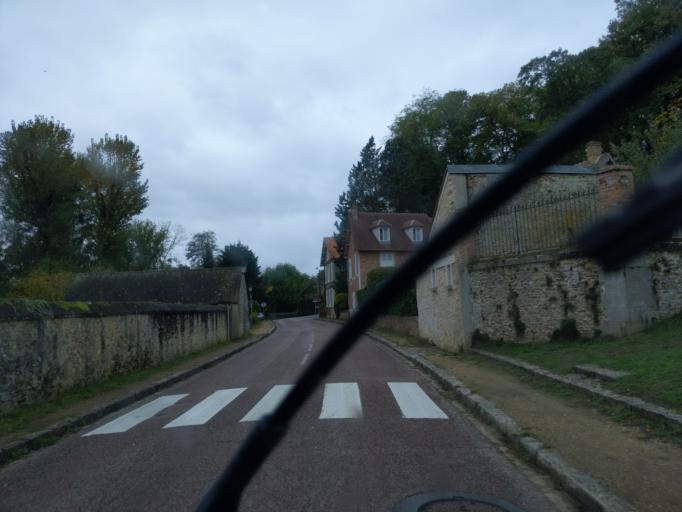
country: FR
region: Ile-de-France
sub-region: Departement des Yvelines
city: Bullion
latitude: 48.6378
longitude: 1.9530
